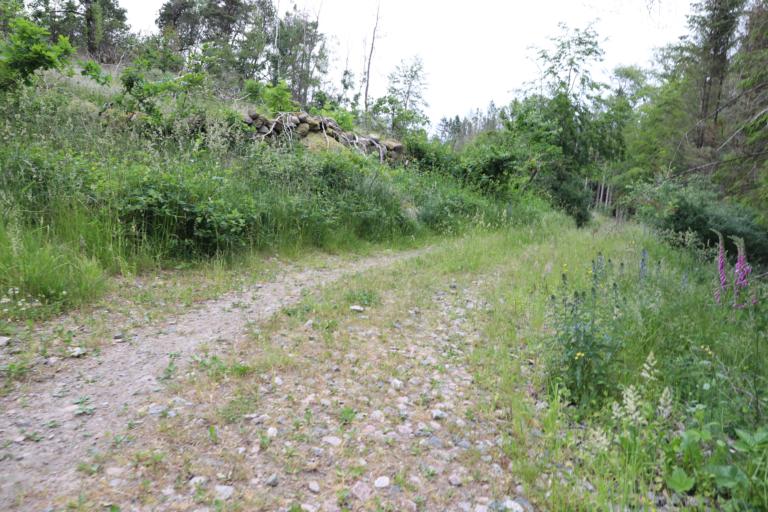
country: SE
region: Halland
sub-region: Varbergs Kommun
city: Varberg
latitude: 57.1666
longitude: 12.2623
